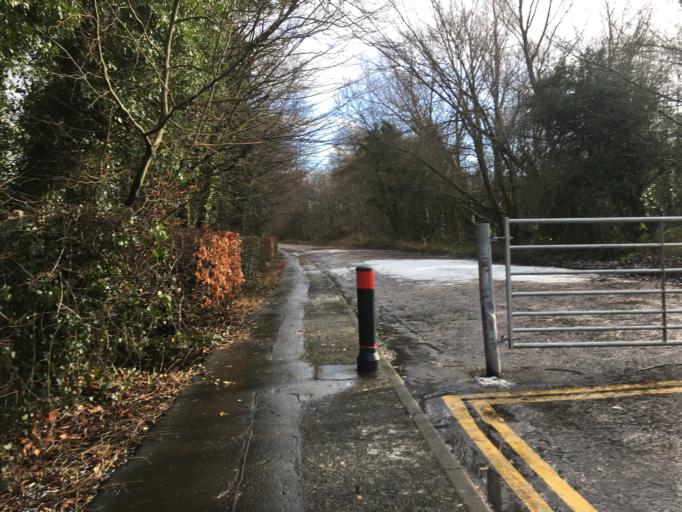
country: GB
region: Scotland
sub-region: Stirling
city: Bridge of Allan
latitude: 56.1363
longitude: -3.9750
